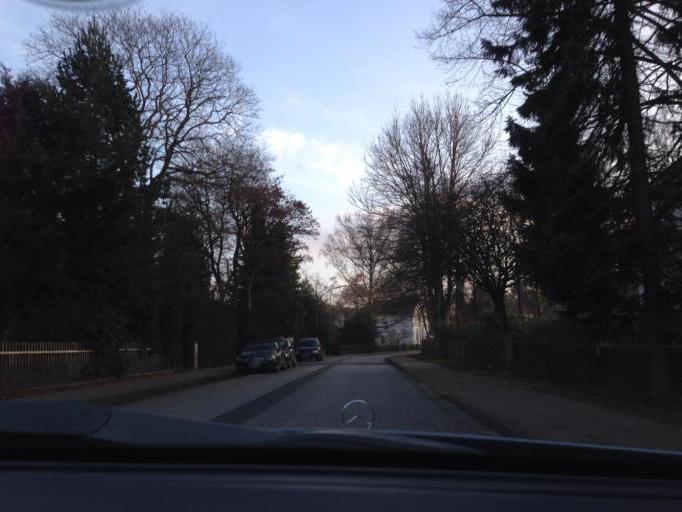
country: DE
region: Schleswig-Holstein
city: Barsbuettel
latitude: 53.6009
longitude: 10.1614
